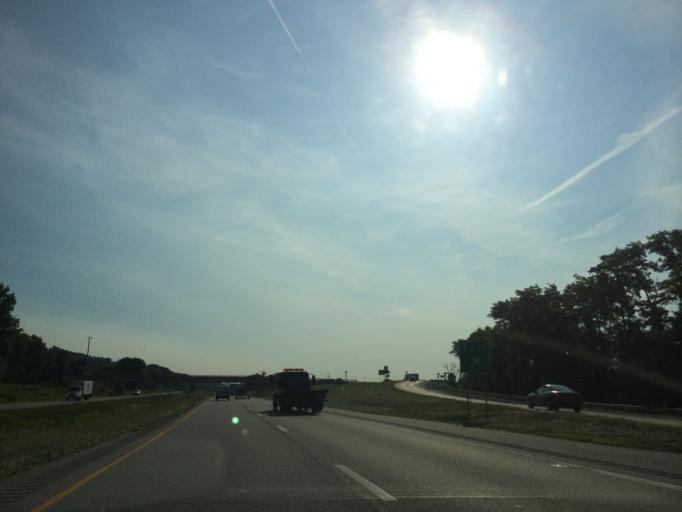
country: US
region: Pennsylvania
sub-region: York County
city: Wrightsville
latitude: 40.0271
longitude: -76.5559
